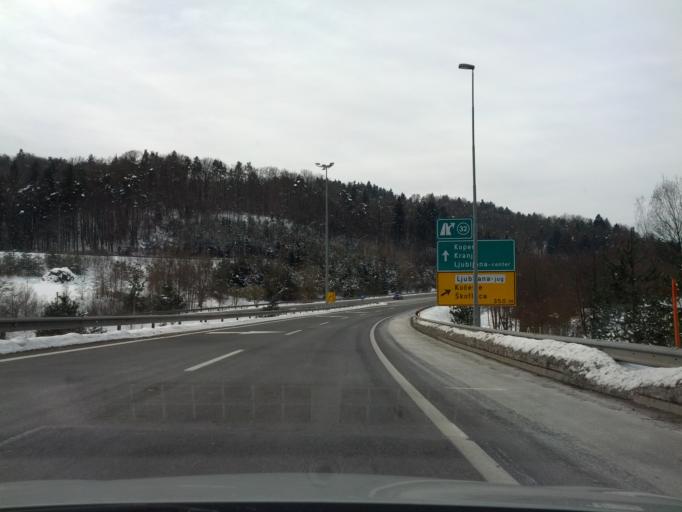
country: SI
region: Skofljica
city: Lavrica
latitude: 46.0145
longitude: 14.5554
